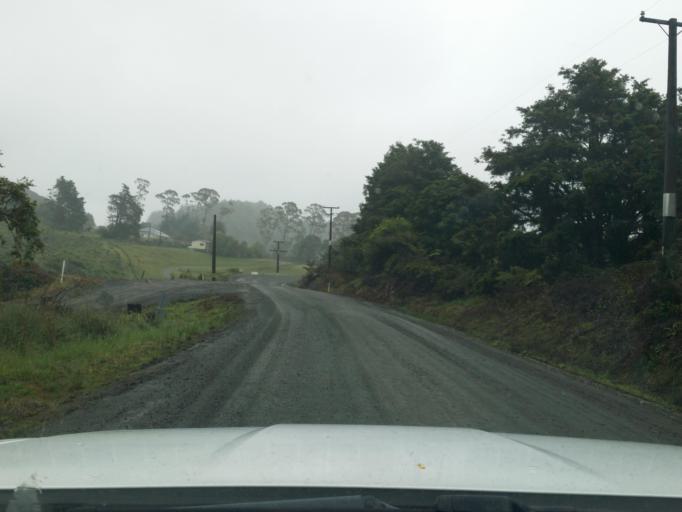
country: NZ
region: Northland
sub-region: Kaipara District
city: Dargaville
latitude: -35.7407
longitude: 173.9080
